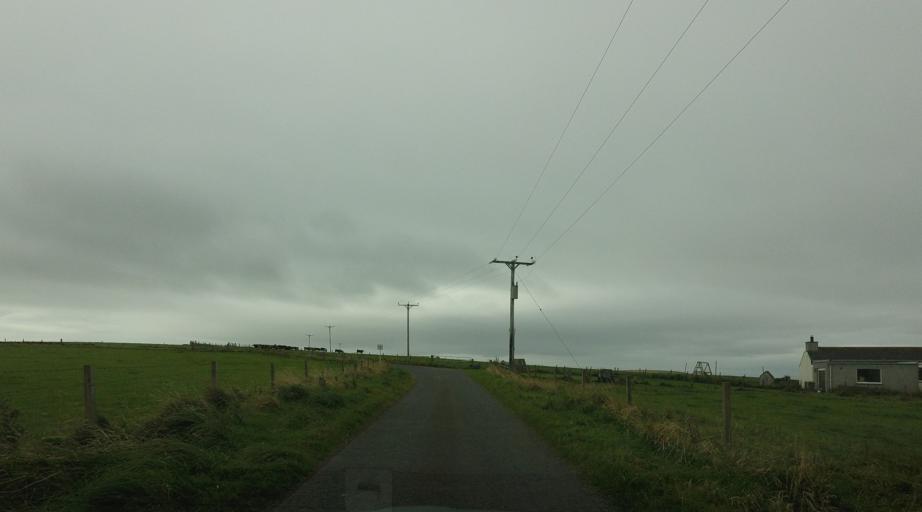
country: GB
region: Scotland
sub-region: Orkney Islands
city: Orkney
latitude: 58.8038
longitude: -2.9410
